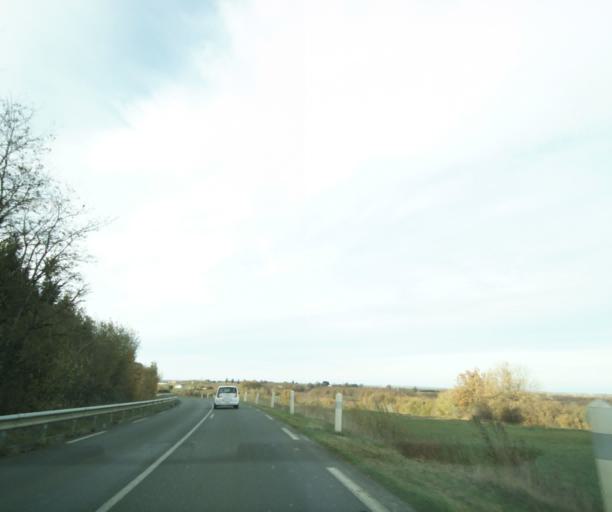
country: FR
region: Midi-Pyrenees
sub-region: Departement du Gers
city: Eauze
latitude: 43.8029
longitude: 0.0991
